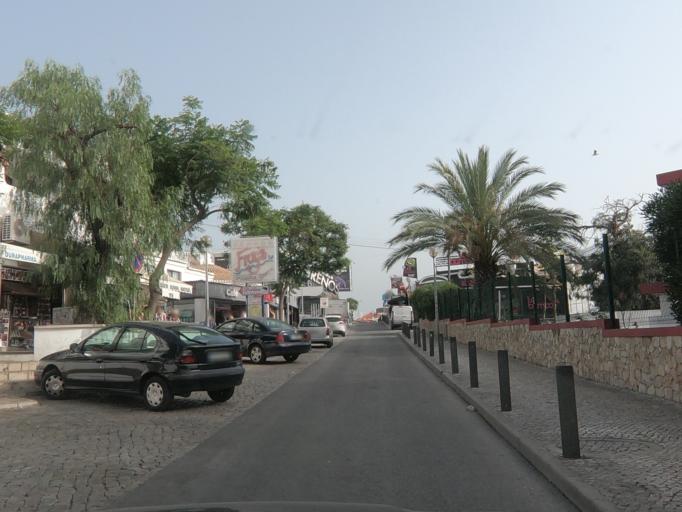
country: PT
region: Faro
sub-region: Albufeira
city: Albufeira
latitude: 37.0908
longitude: -8.2276
